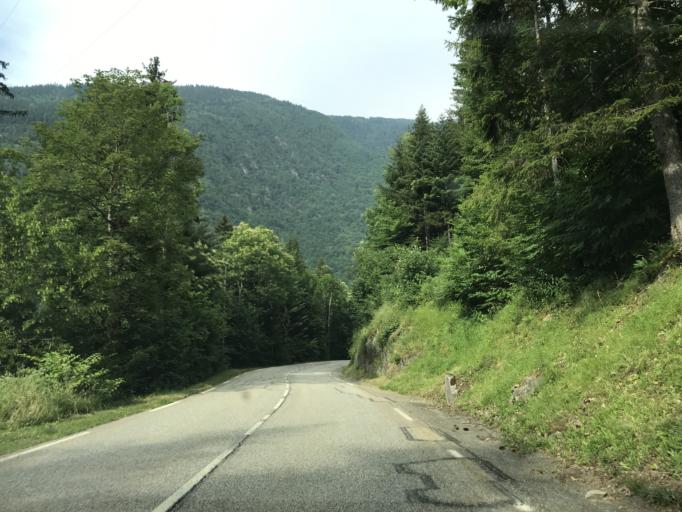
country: FR
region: Rhone-Alpes
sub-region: Departement de l'Isere
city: Allevard
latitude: 45.3797
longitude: 6.0907
